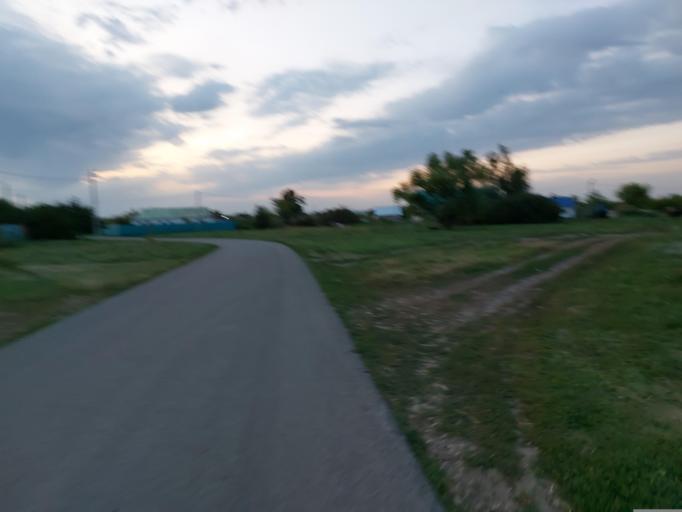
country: RU
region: Lipetsk
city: Dolgorukovo
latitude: 52.3775
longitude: 38.0503
